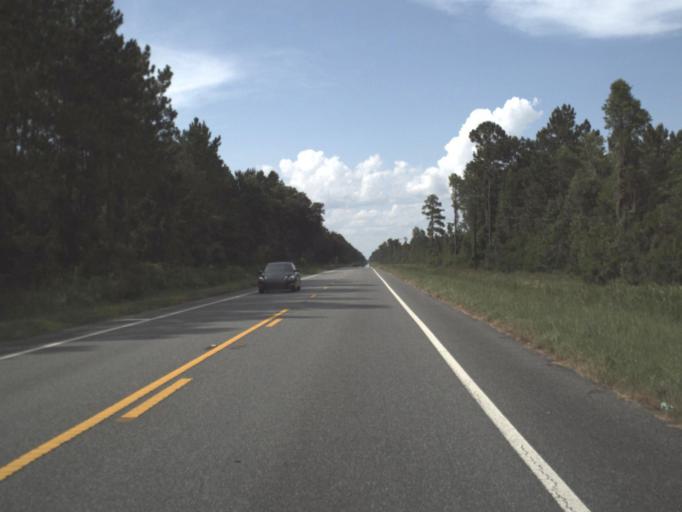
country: US
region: Florida
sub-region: Taylor County
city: Perry
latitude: 30.2199
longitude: -83.6143
